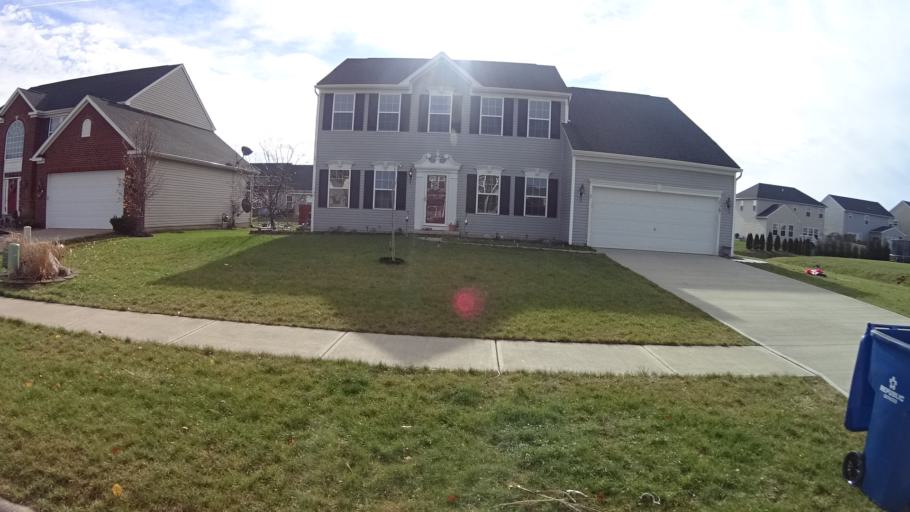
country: US
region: Ohio
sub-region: Lorain County
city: North Ridgeville
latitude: 41.3620
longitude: -82.0522
